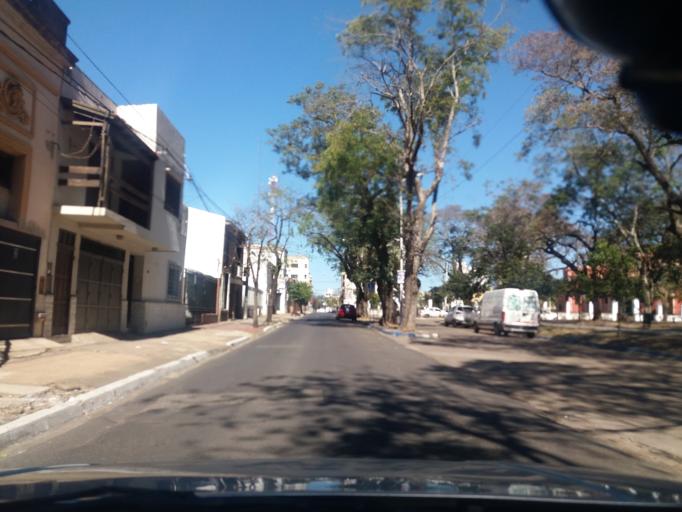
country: AR
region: Corrientes
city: Corrientes
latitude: -27.4711
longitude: -58.8394
